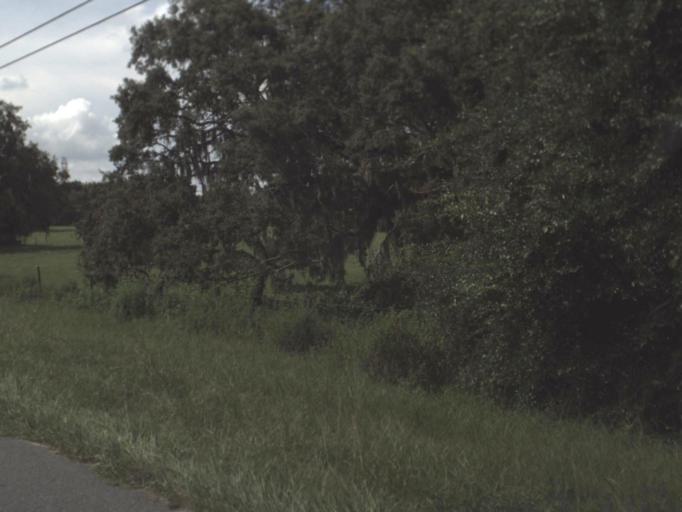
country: US
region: Florida
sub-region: Citrus County
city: Beverly Hills
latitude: 28.9583
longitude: -82.4147
